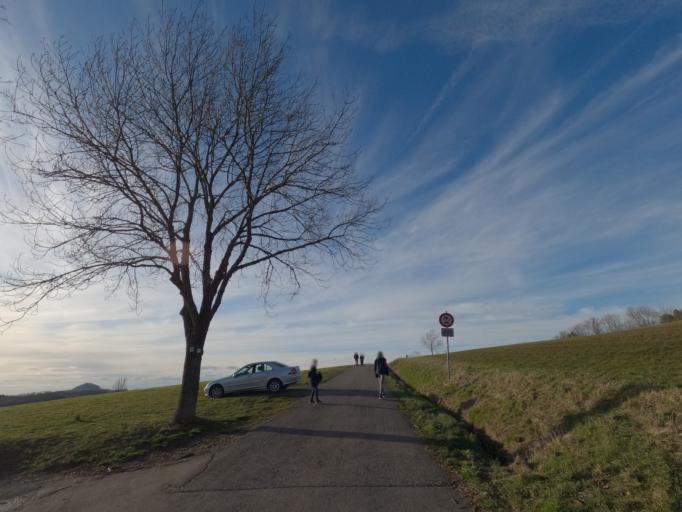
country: DE
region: Baden-Wuerttemberg
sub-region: Regierungsbezirk Stuttgart
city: Waldstetten
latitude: 48.7381
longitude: 9.8117
